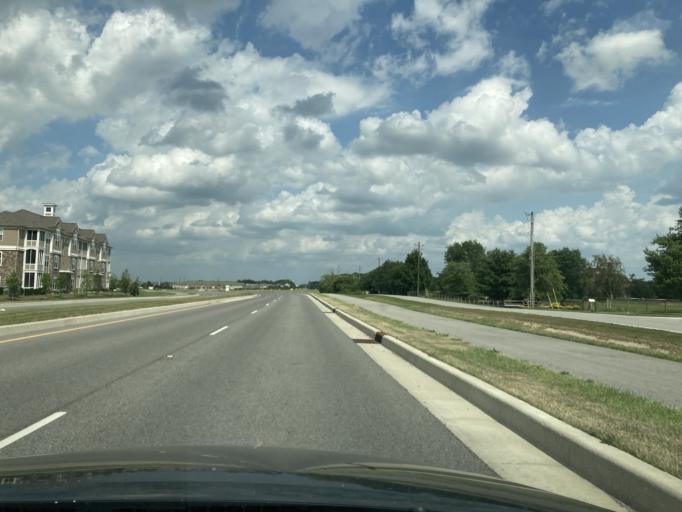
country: US
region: Indiana
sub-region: Hamilton County
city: Carmel
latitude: 39.9994
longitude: -86.1891
